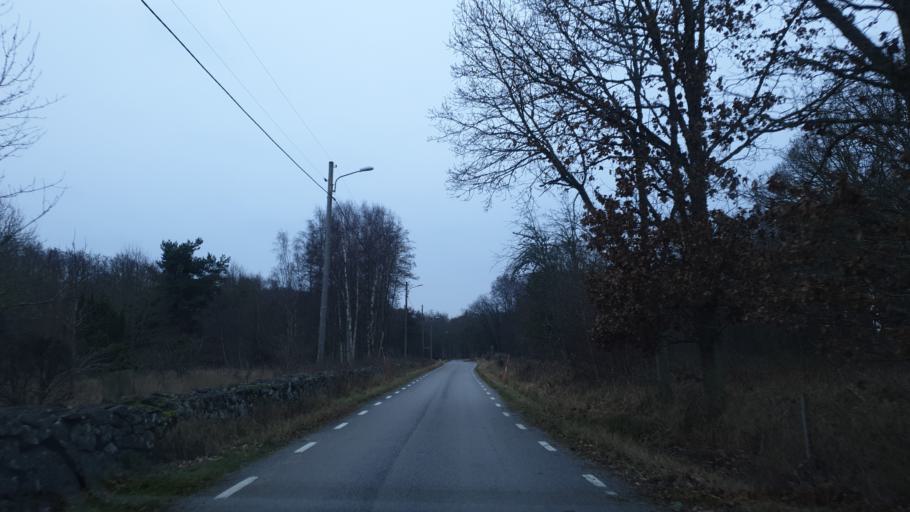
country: SE
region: Blekinge
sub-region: Karlskrona Kommun
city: Karlskrona
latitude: 56.1071
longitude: 15.6111
